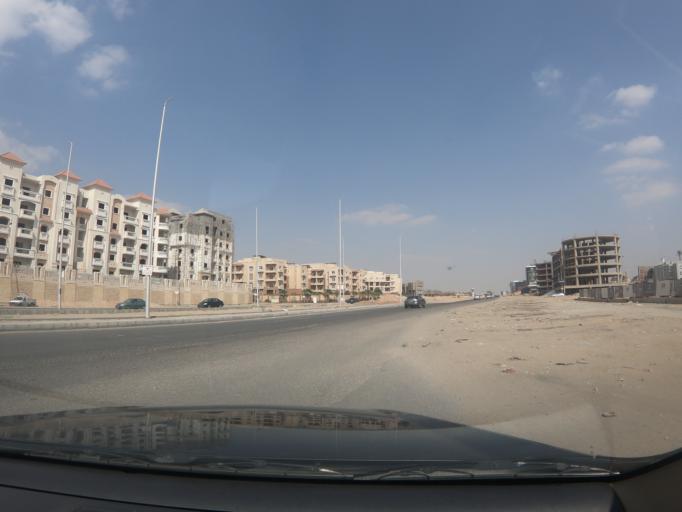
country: EG
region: Muhafazat al Qalyubiyah
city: Al Khankah
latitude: 30.0284
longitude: 31.4770
